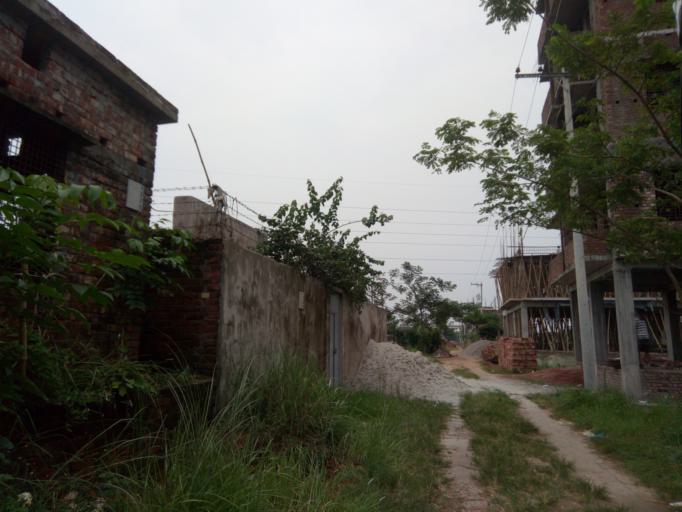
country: BD
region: Dhaka
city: Azimpur
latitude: 23.7409
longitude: 90.3369
